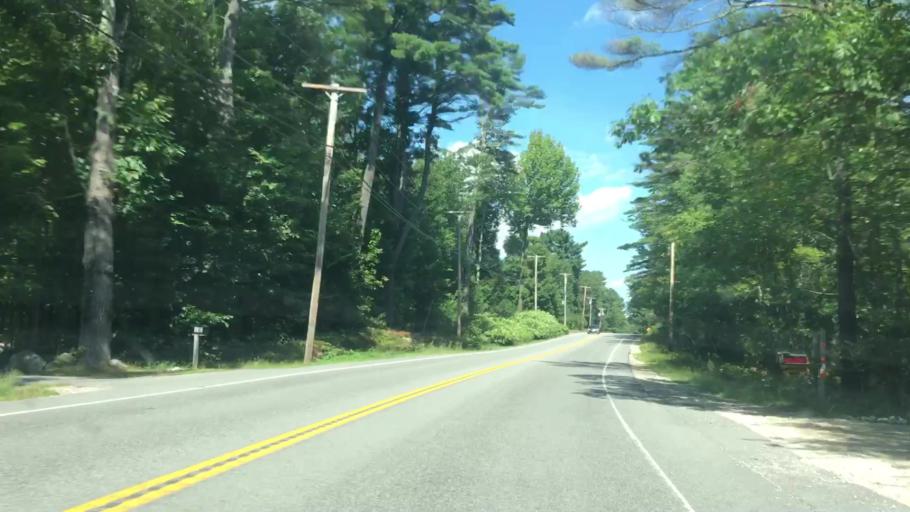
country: US
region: Maine
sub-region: Cumberland County
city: New Gloucester
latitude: 43.9321
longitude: -70.3088
